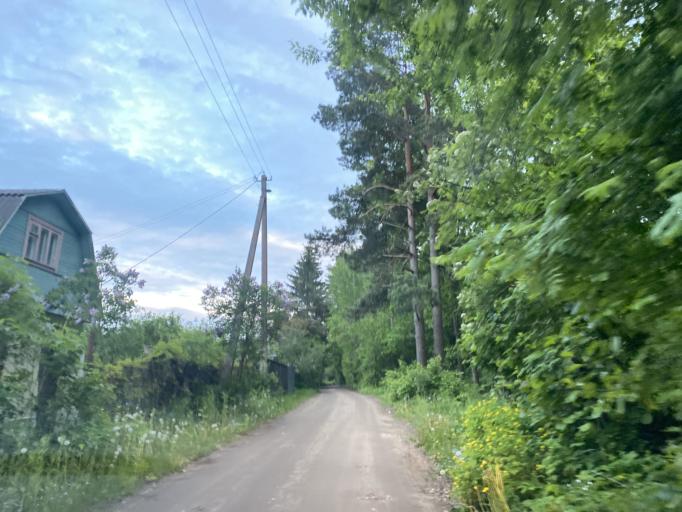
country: BY
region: Minsk
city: Rudzyensk
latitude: 53.6077
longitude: 27.7885
